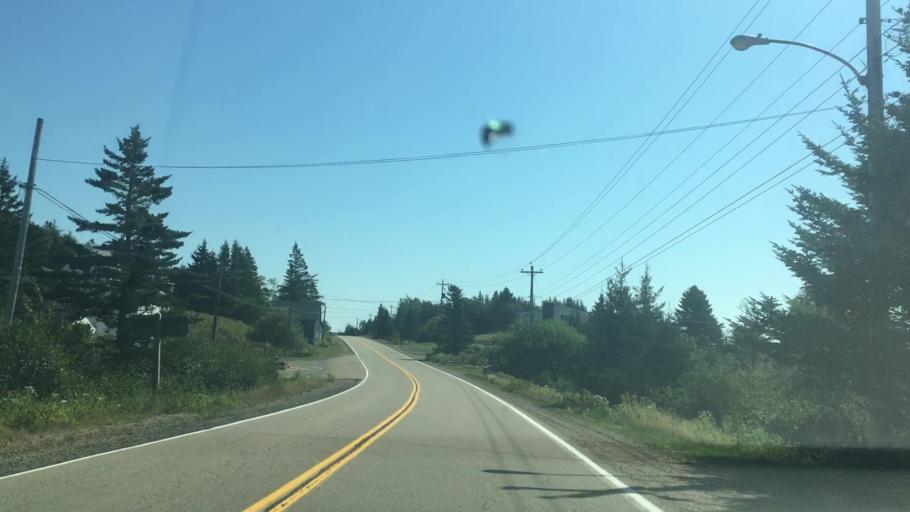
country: CA
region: Nova Scotia
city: Antigonish
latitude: 45.0251
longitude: -62.0255
